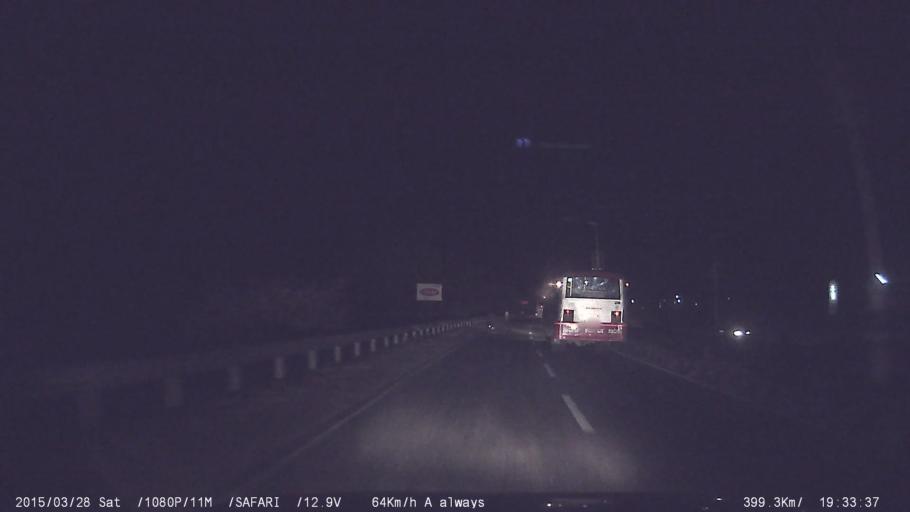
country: IN
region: Karnataka
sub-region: Mandya
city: Shrirangapattana
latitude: 12.4260
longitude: 76.6946
